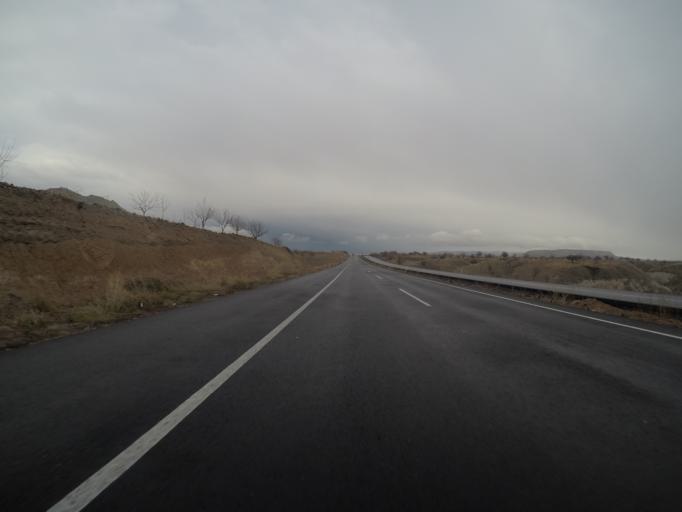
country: TR
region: Nevsehir
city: Goereme
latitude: 38.6827
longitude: 34.7971
